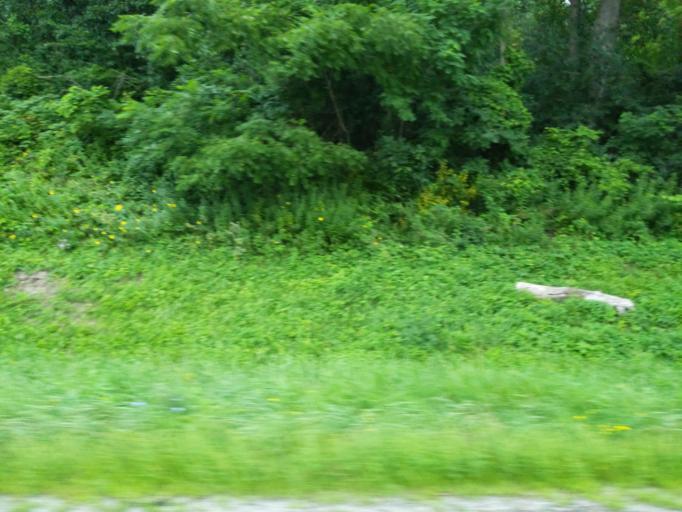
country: US
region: Wisconsin
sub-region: Dane County
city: Mazomanie
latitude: 43.2133
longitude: -89.7501
